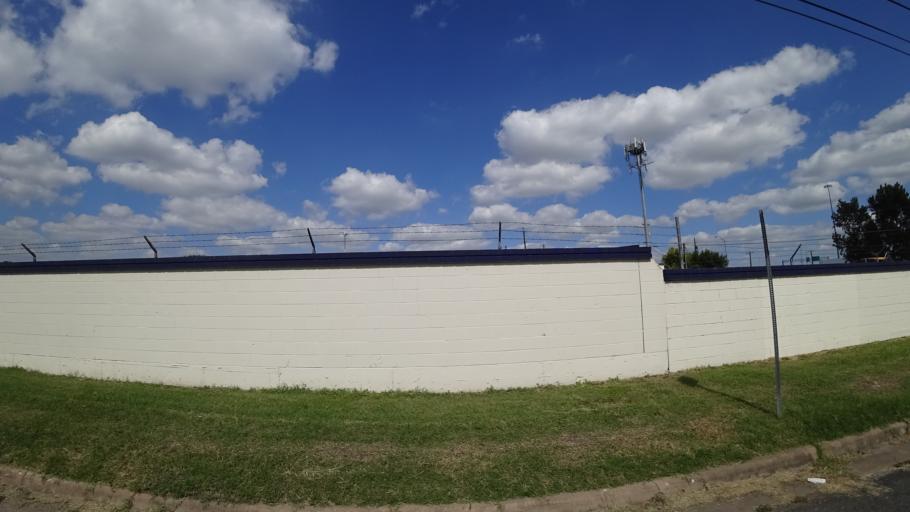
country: US
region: Texas
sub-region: Travis County
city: Austin
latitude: 30.3199
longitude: -97.7167
